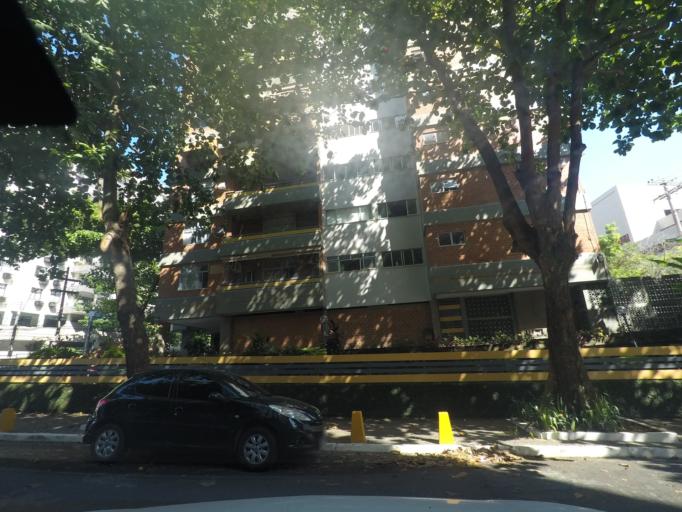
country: BR
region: Rio de Janeiro
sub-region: Niteroi
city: Niteroi
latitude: -22.9064
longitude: -43.1323
